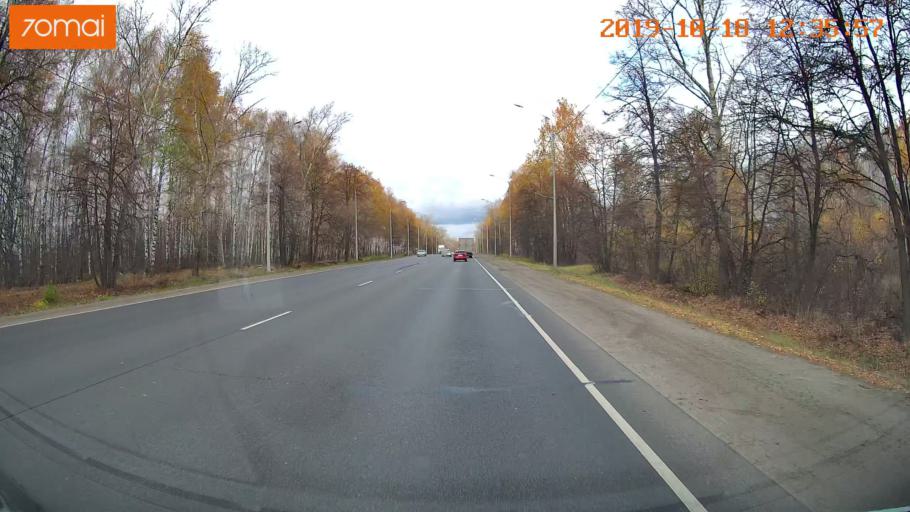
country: RU
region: Rjazan
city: Ryazan'
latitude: 54.6300
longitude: 39.6348
